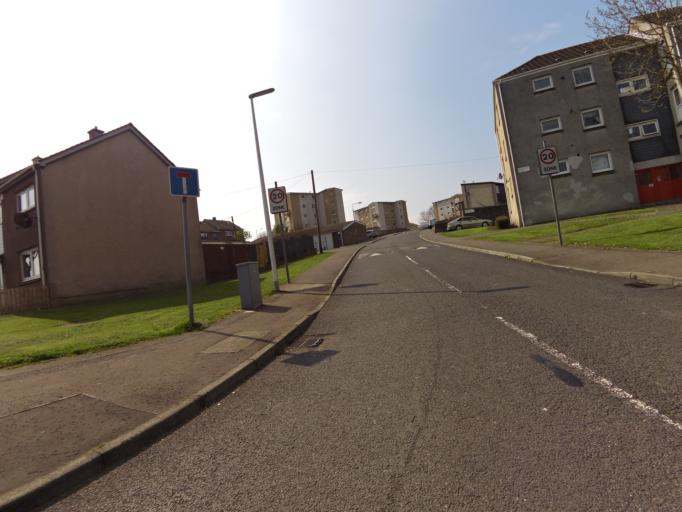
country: GB
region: Scotland
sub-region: Fife
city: Kirkcaldy
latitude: 56.0980
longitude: -3.1649
